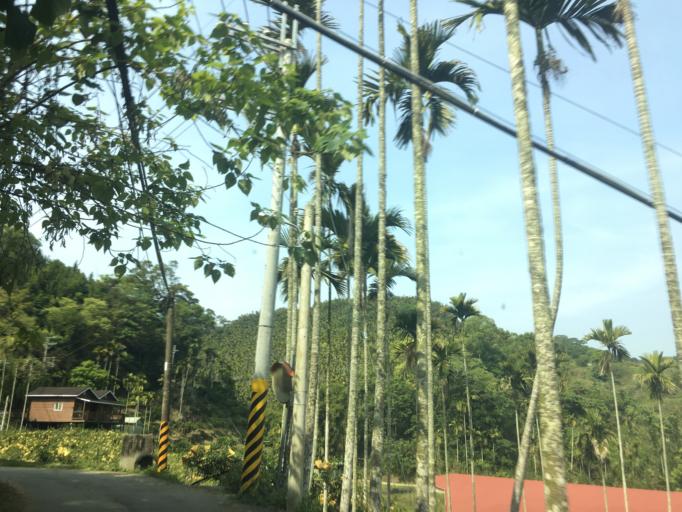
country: TW
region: Taiwan
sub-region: Taichung City
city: Taichung
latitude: 24.1566
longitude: 120.8290
